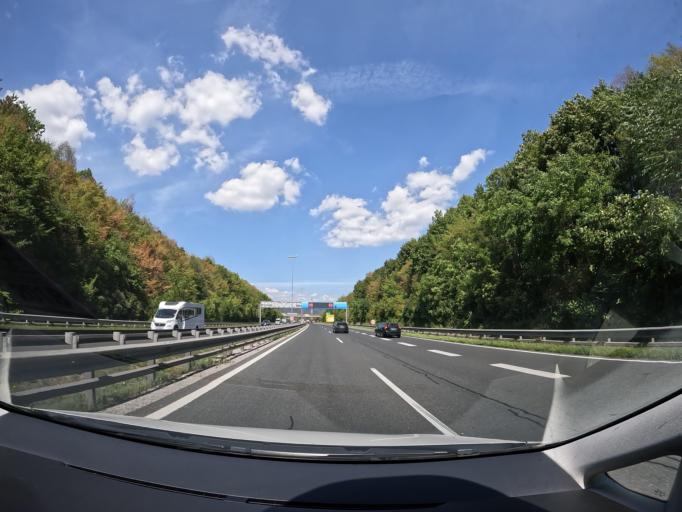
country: SI
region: Medvode
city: Zgornje Pirnice
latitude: 46.1119
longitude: 14.4517
